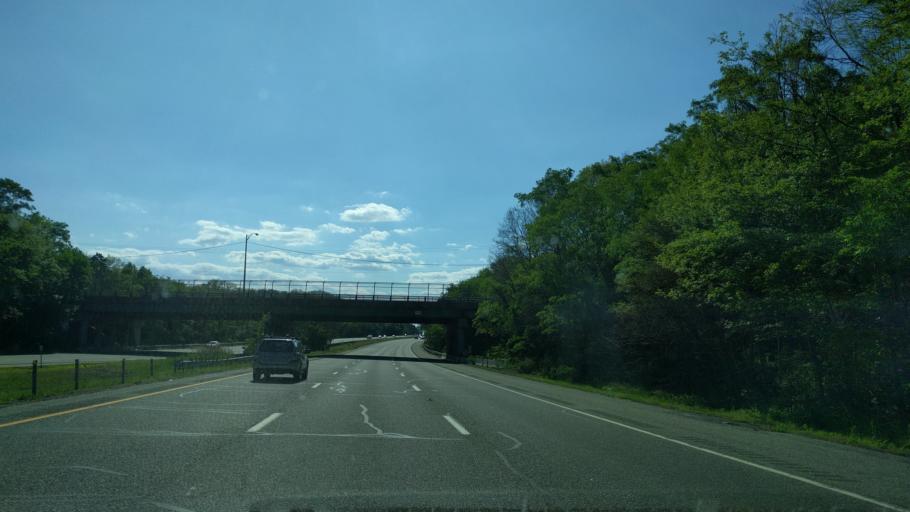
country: US
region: Rhode Island
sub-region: Providence County
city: Cumberland
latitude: 41.9507
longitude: -71.4014
